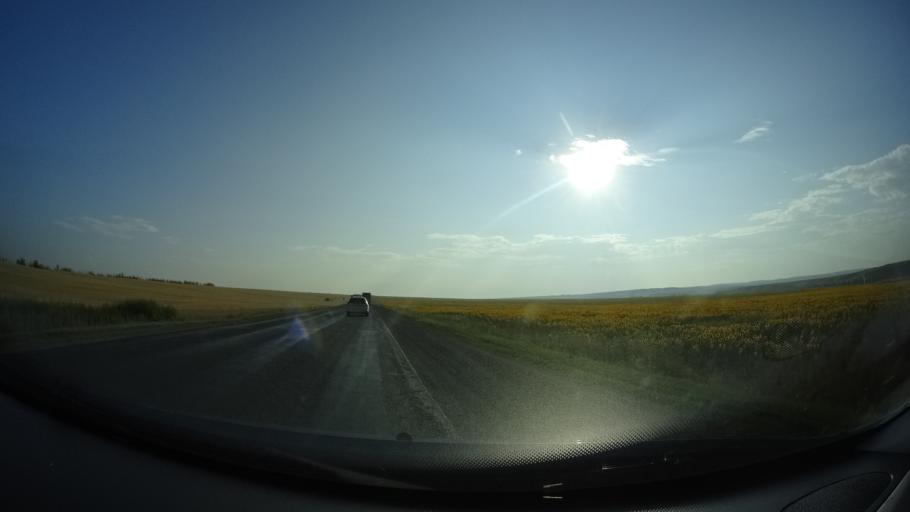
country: RU
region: Orenburg
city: Severnoye
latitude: 54.1227
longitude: 52.5524
